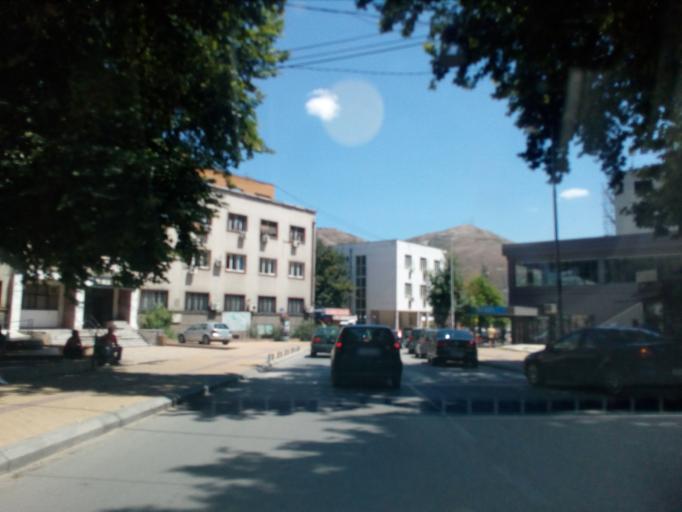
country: MK
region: Veles
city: Veles
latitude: 41.7174
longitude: 21.7817
